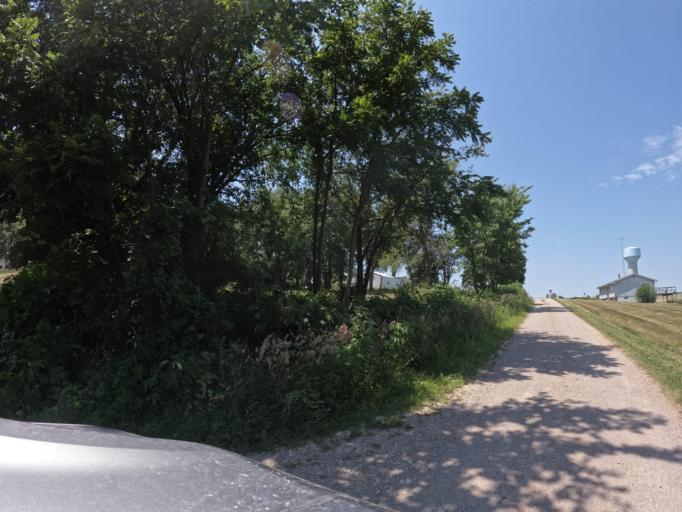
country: US
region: Iowa
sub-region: Appanoose County
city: Centerville
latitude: 40.7863
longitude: -92.9051
